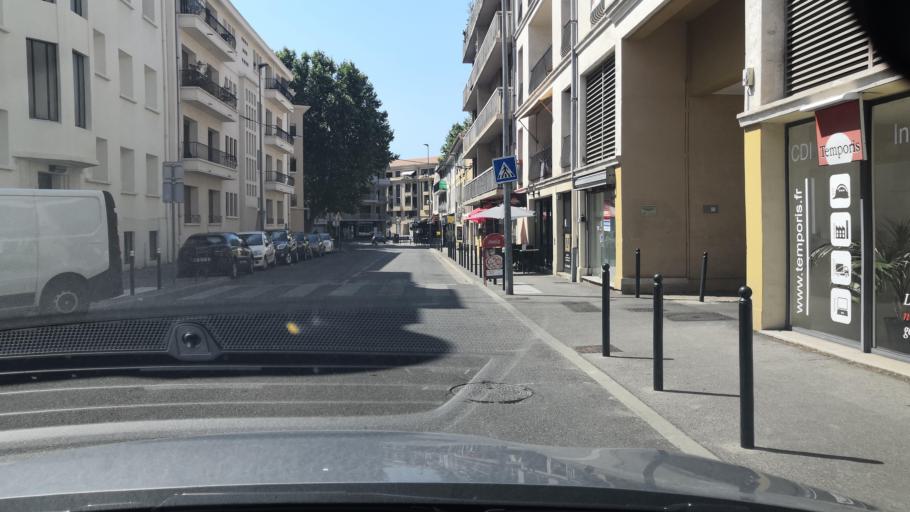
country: FR
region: Provence-Alpes-Cote d'Azur
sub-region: Departement des Bouches-du-Rhone
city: Aix-en-Provence
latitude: 43.5226
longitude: 5.4509
